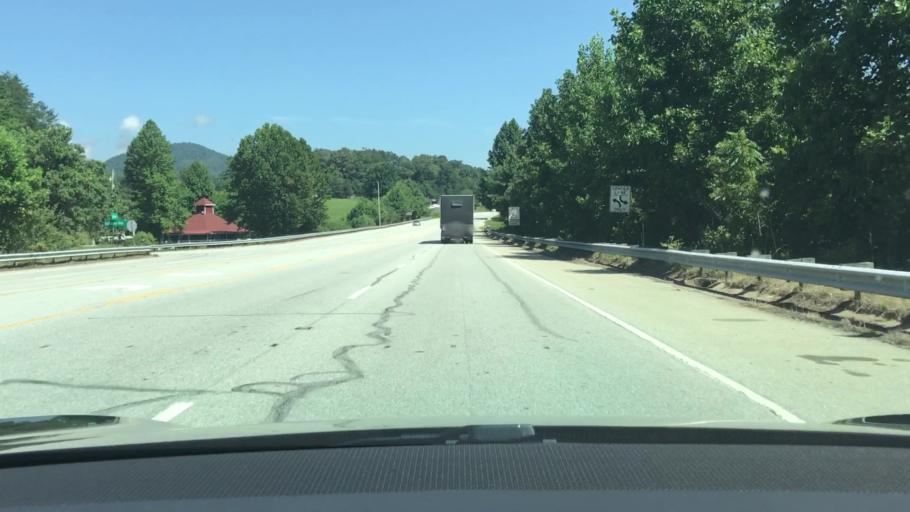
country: US
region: Georgia
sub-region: Rabun County
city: Mountain City
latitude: 34.9983
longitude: -83.3821
